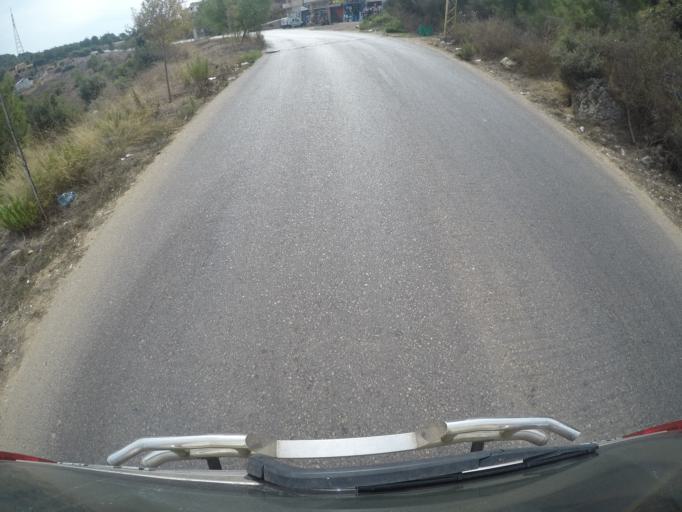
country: LB
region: Mont-Liban
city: Beit ed Dine
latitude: 33.7351
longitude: 35.4851
